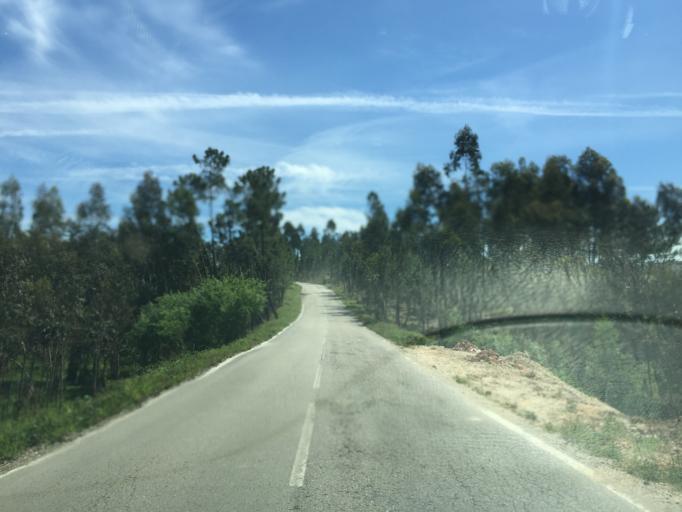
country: PT
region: Leiria
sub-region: Pombal
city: Lourical
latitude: 40.0637
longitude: -8.7109
